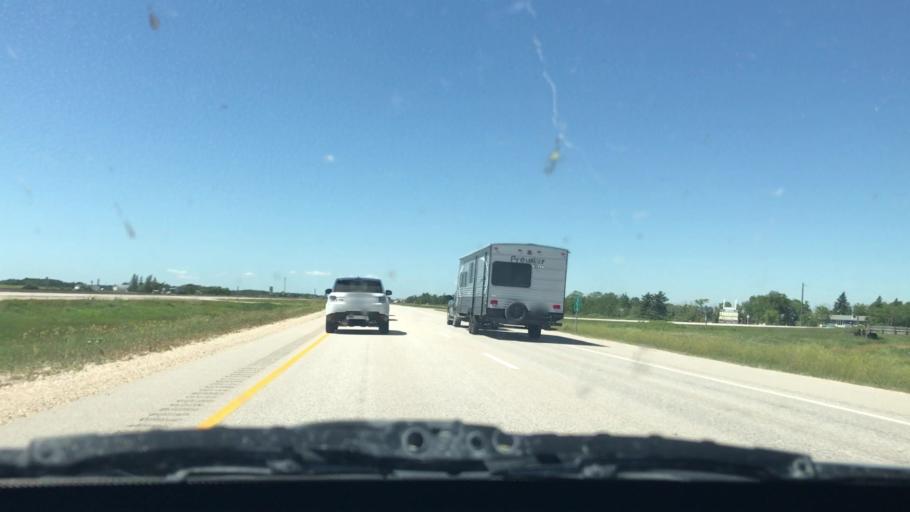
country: CA
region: Manitoba
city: Niverville
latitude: 49.8106
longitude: -96.9120
